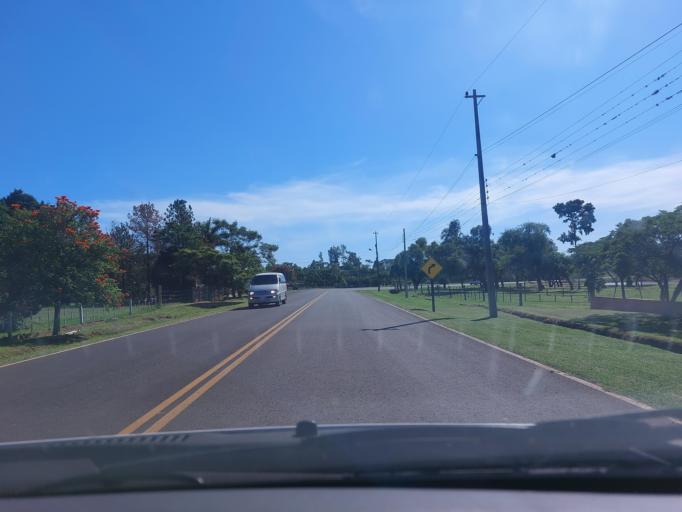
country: PY
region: San Pedro
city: Itacurubi del Rosario
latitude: -24.6075
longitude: -56.7910
